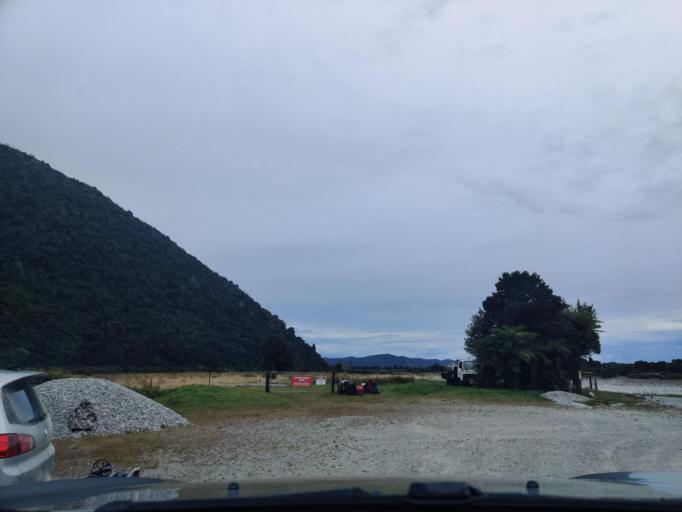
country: NZ
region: West Coast
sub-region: Westland District
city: Hokitika
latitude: -43.2937
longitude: 170.4125
